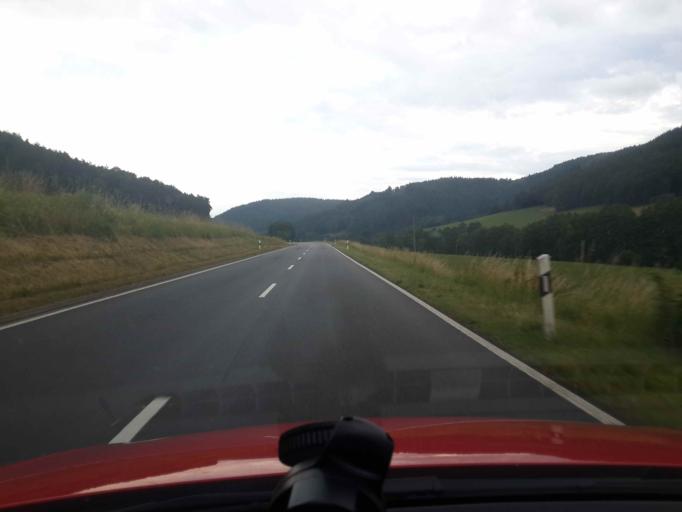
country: DE
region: Bavaria
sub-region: Regierungsbezirk Unterfranken
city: Kirchzell
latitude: 49.6123
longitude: 9.1991
